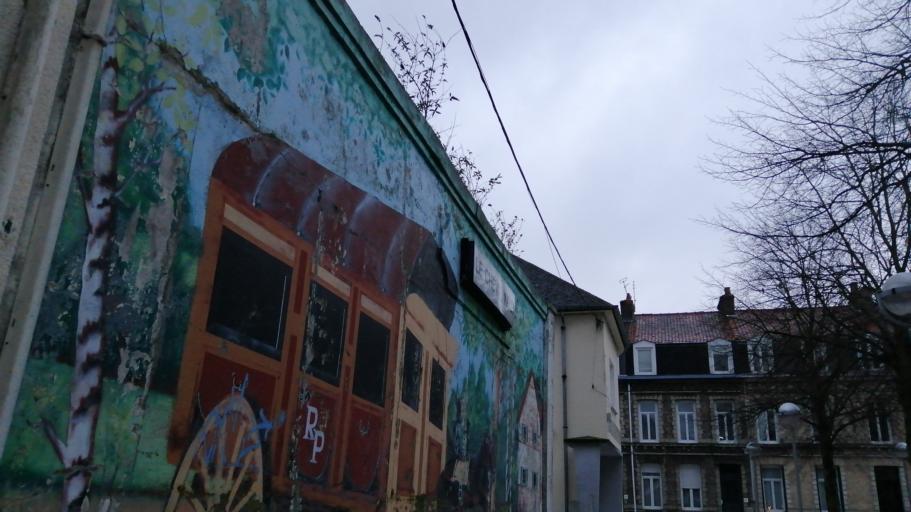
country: FR
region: Nord-Pas-de-Calais
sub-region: Departement du Pas-de-Calais
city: Calais
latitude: 50.9439
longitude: 1.8598
